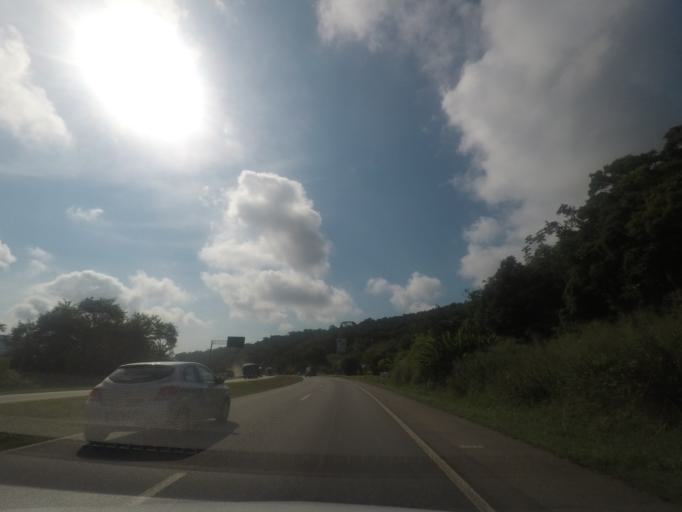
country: BR
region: Parana
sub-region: Antonina
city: Antonina
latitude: -25.5452
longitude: -48.7818
